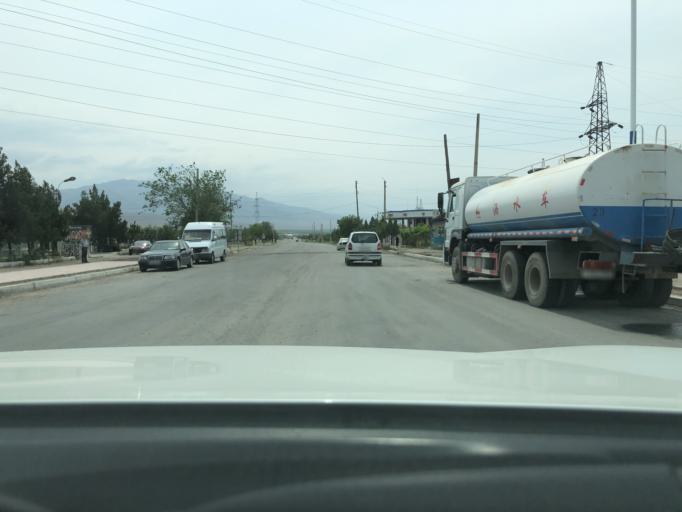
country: TJ
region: Viloyati Sughd
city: Konibodom
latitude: 40.2768
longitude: 70.4436
